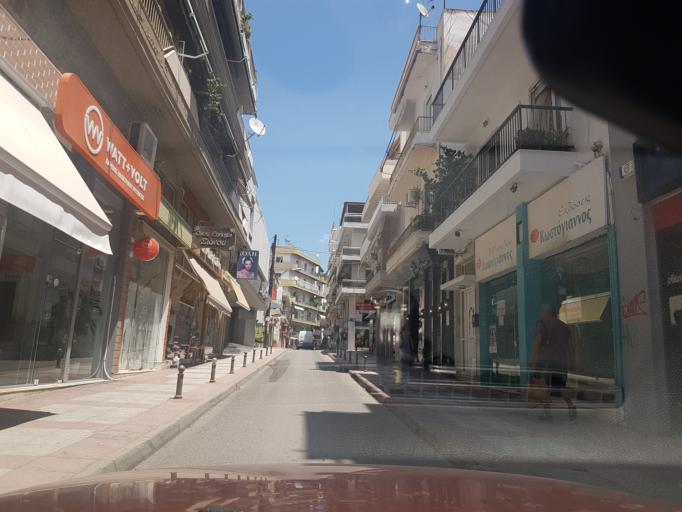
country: GR
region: Central Greece
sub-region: Nomos Evvoias
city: Chalkida
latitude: 38.4677
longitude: 23.5987
